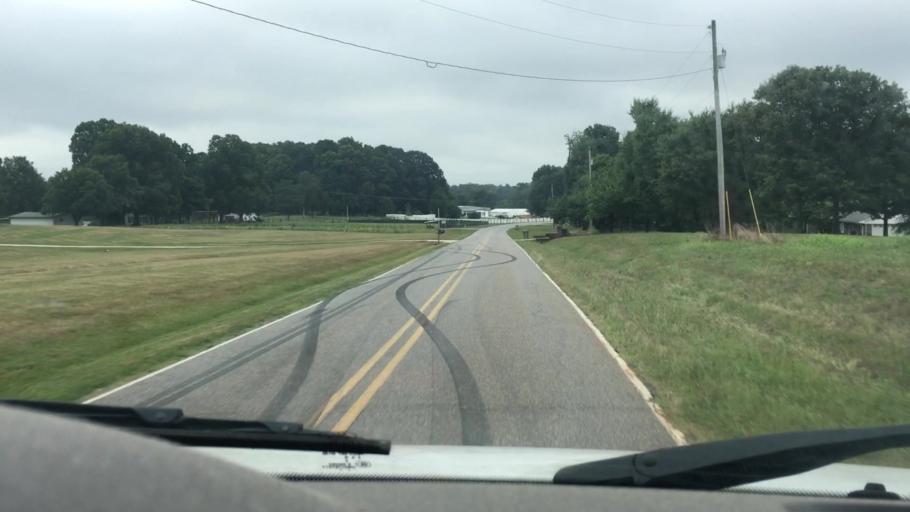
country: US
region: North Carolina
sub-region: Gaston County
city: Davidson
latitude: 35.5313
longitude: -80.8292
